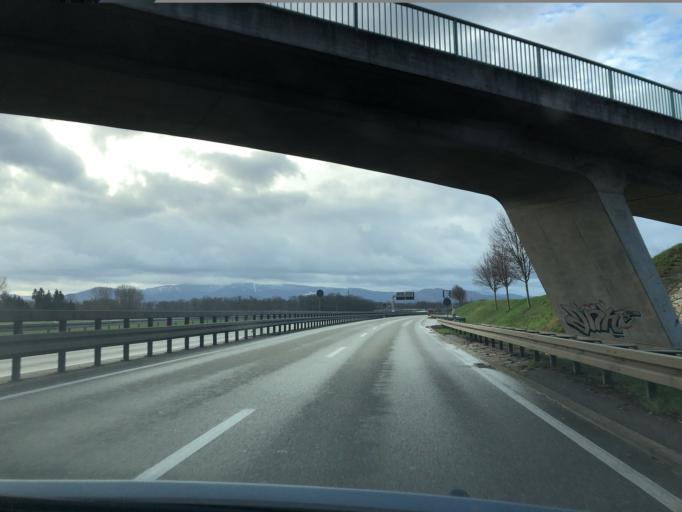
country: DE
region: Baden-Wuerttemberg
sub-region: Freiburg Region
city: Umkirch
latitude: 48.0355
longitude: 7.7779
